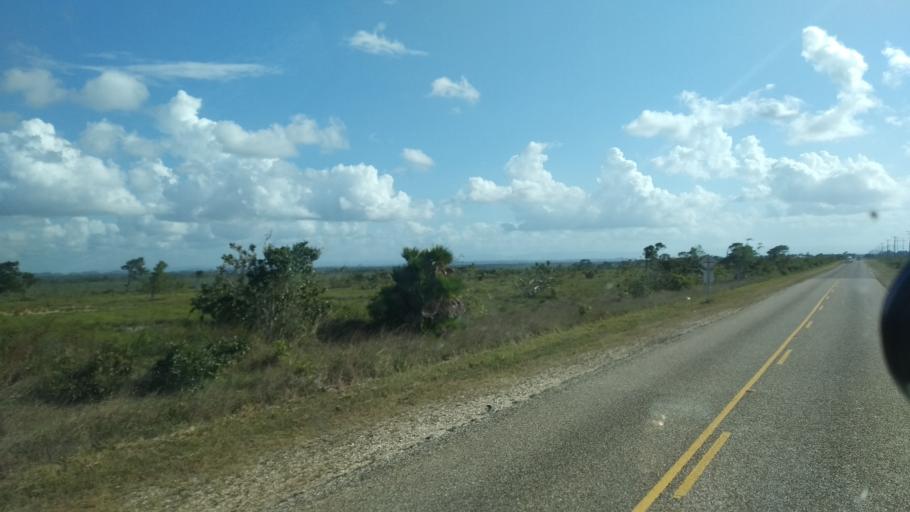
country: BZ
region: Cayo
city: Belmopan
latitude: 17.4029
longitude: -88.5039
